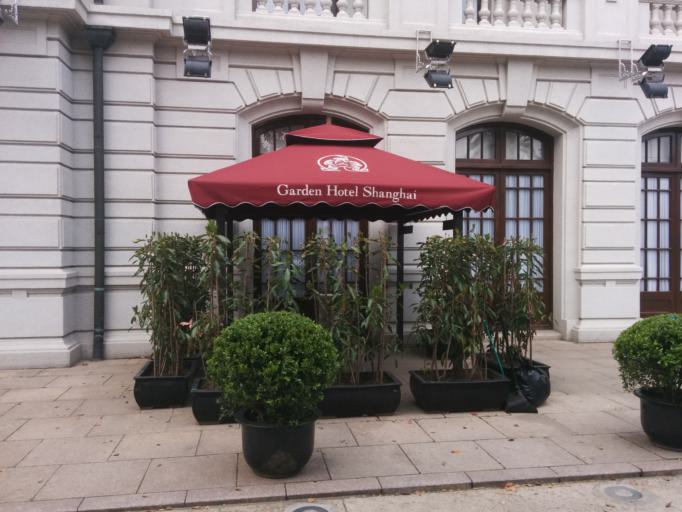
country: CN
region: Shanghai Shi
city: Shanghai
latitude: 31.2214
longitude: 121.4549
